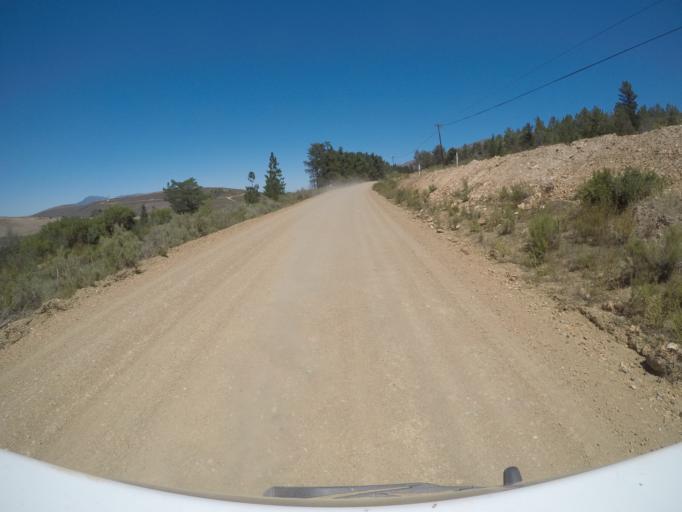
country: ZA
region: Western Cape
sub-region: Overberg District Municipality
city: Caledon
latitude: -34.1728
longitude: 19.2288
